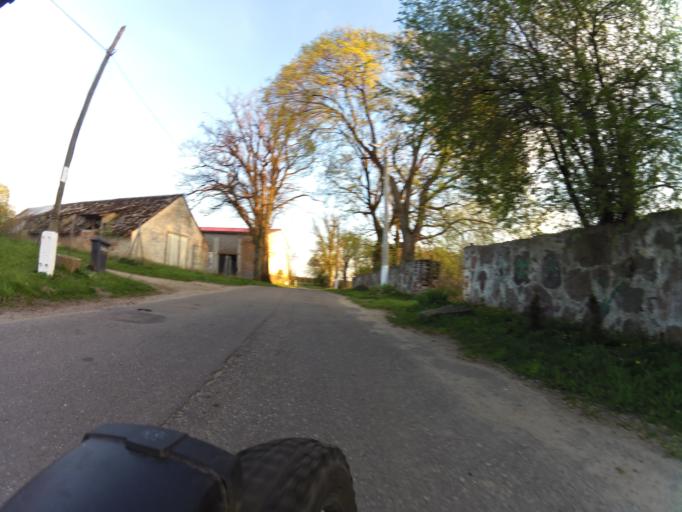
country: PL
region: West Pomeranian Voivodeship
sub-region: Powiat lobeski
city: Lobez
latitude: 53.6972
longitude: 15.6447
